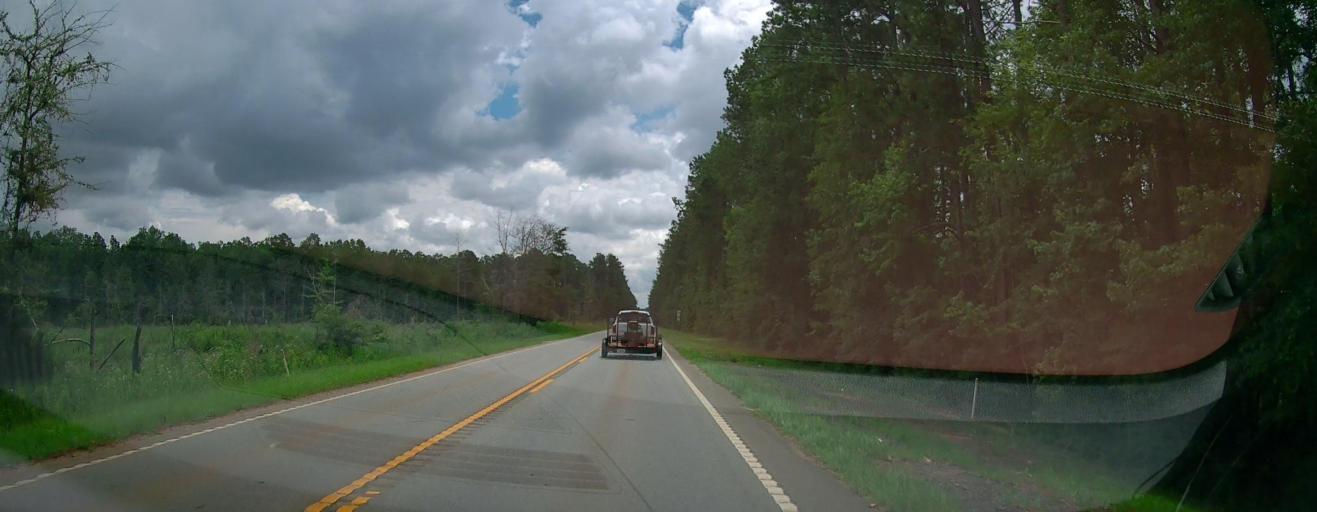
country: US
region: Georgia
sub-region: Houston County
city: Perry
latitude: 32.4414
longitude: -83.5890
